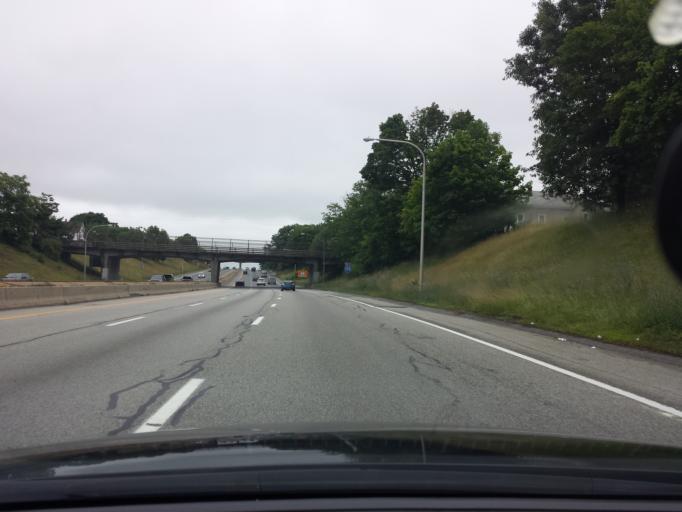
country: US
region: Rhode Island
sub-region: Providence County
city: East Providence
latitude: 41.8177
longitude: -71.3796
